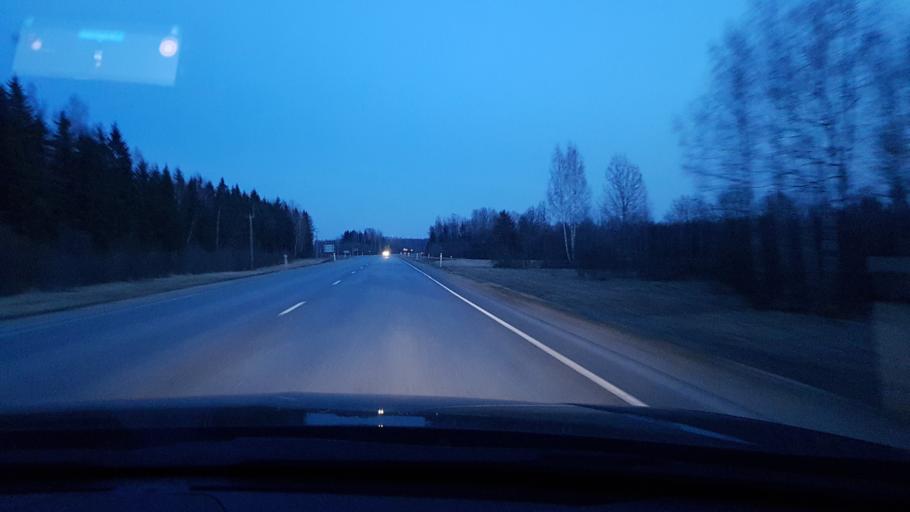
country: EE
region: Tartu
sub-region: Puhja vald
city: Puhja
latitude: 58.5189
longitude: 26.3157
